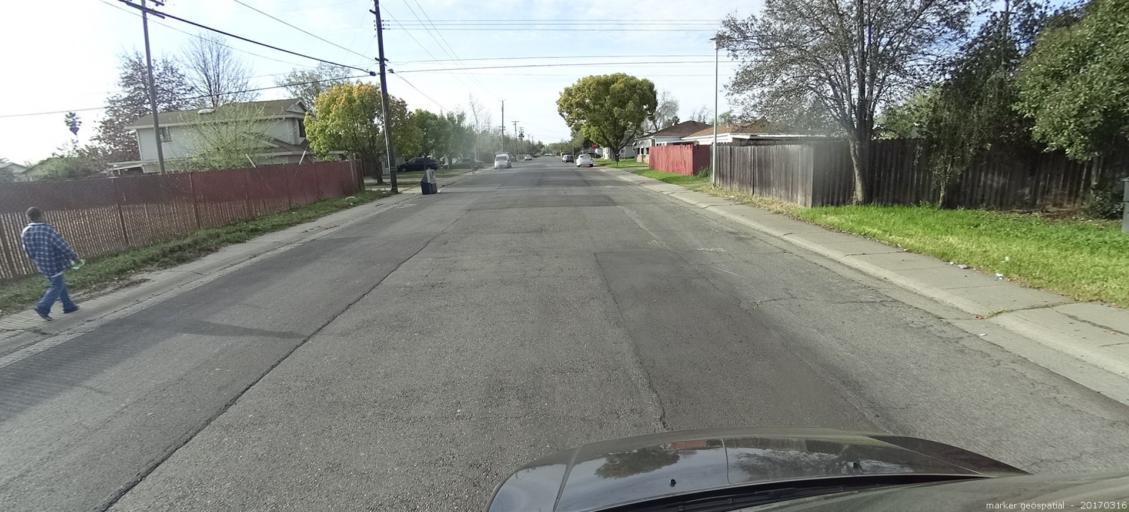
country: US
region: California
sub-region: Sacramento County
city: Parkway
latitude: 38.5077
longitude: -121.4788
